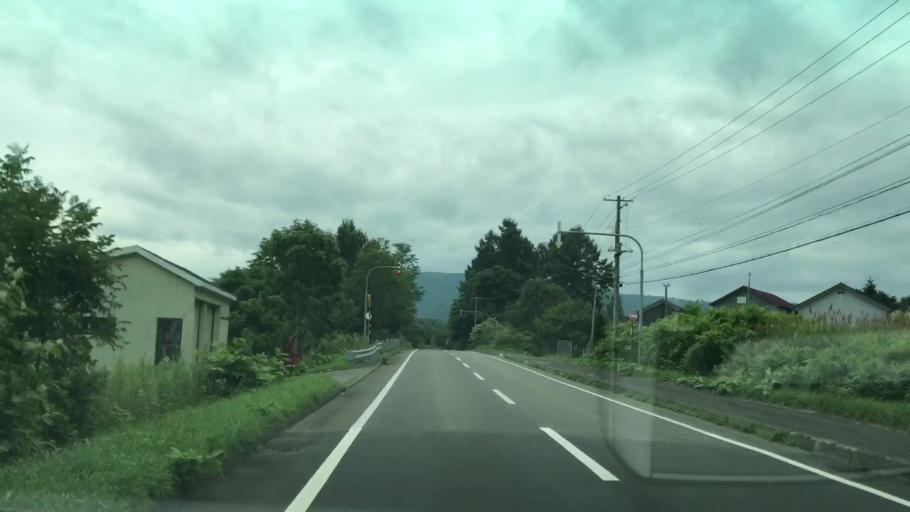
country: JP
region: Hokkaido
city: Yoichi
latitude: 43.0675
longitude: 140.8196
